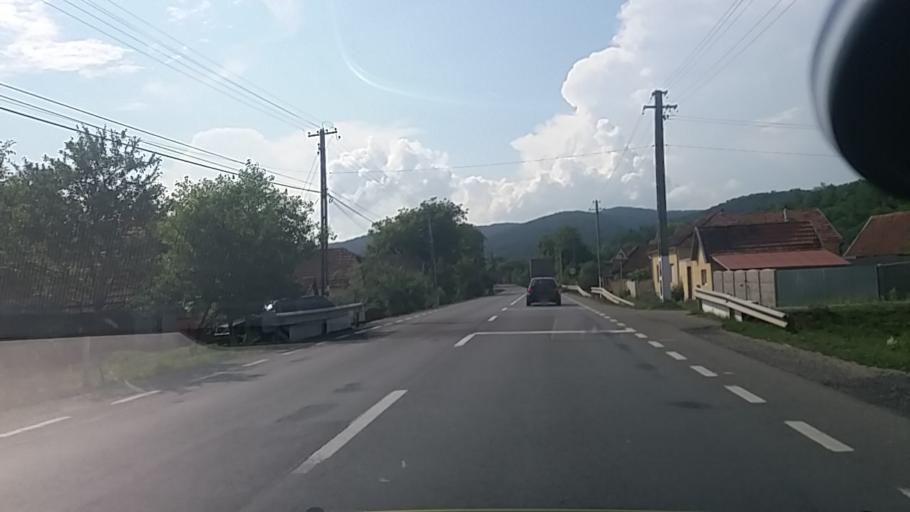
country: RO
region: Arad
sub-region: Comuna Barzava
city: Barzava
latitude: 46.1091
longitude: 21.9803
